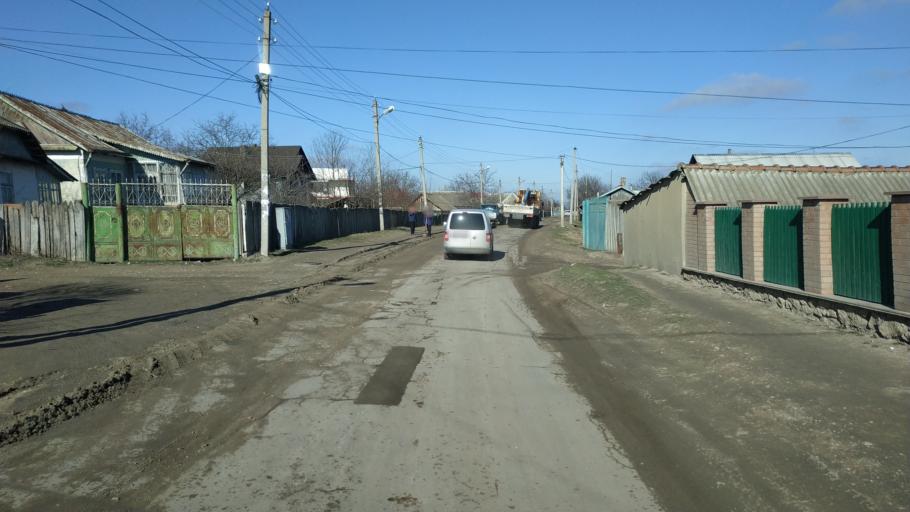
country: MD
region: Hincesti
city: Hincesti
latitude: 46.9330
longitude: 28.6453
